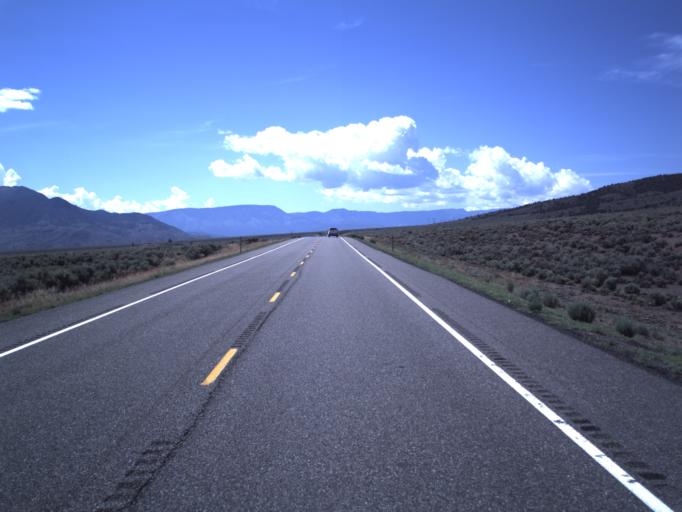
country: US
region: Utah
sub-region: Piute County
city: Junction
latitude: 38.3611
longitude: -112.2229
